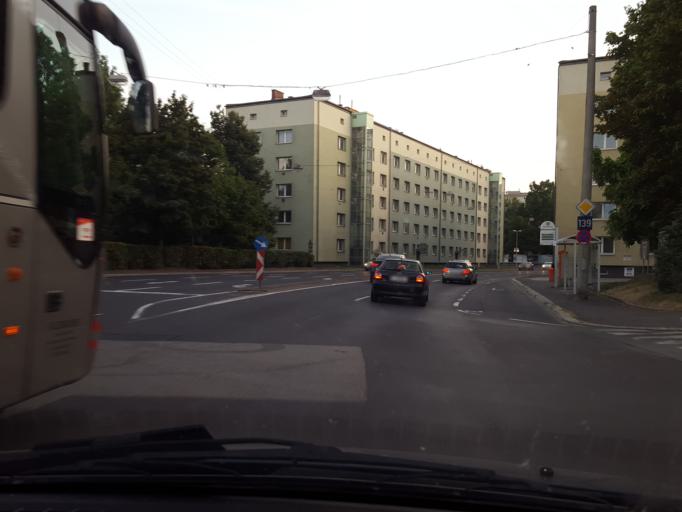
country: AT
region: Upper Austria
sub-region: Linz Stadt
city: Linz
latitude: 48.2851
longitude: 14.2858
